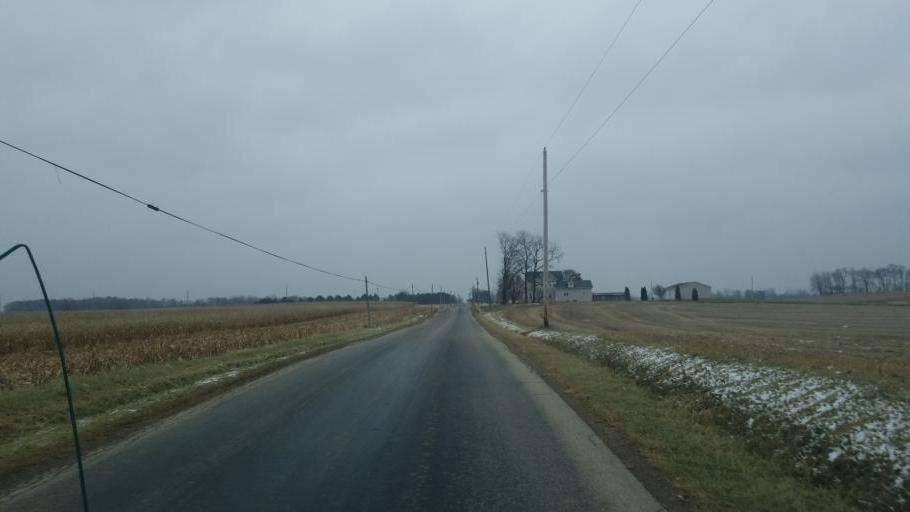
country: US
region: Ohio
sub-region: Richland County
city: Shelby
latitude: 40.9085
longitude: -82.6913
